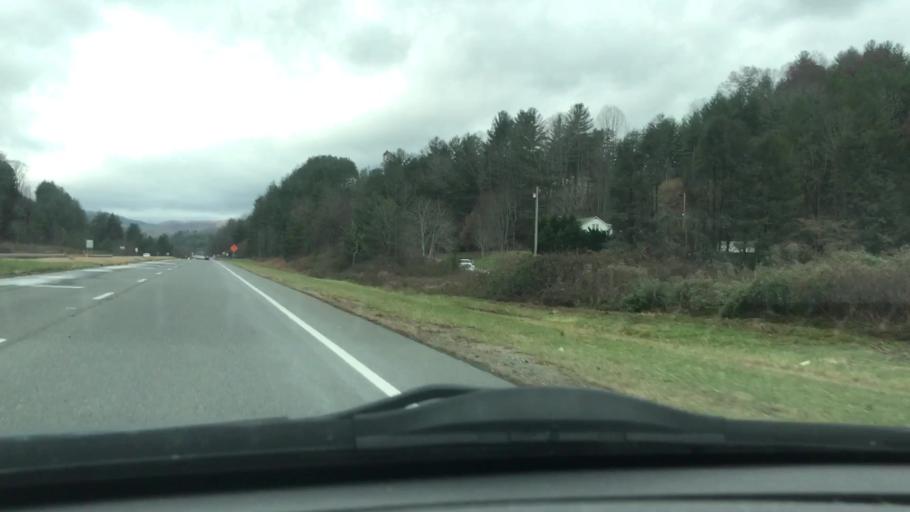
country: US
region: North Carolina
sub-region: Yancey County
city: Burnsville
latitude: 35.9135
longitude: -82.4079
